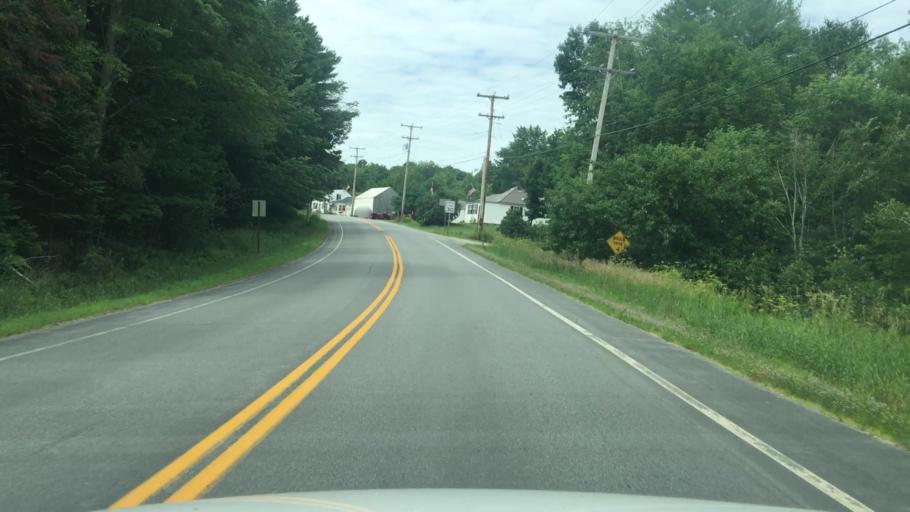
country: US
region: Maine
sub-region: Waldo County
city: Troy
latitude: 44.5330
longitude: -69.2902
